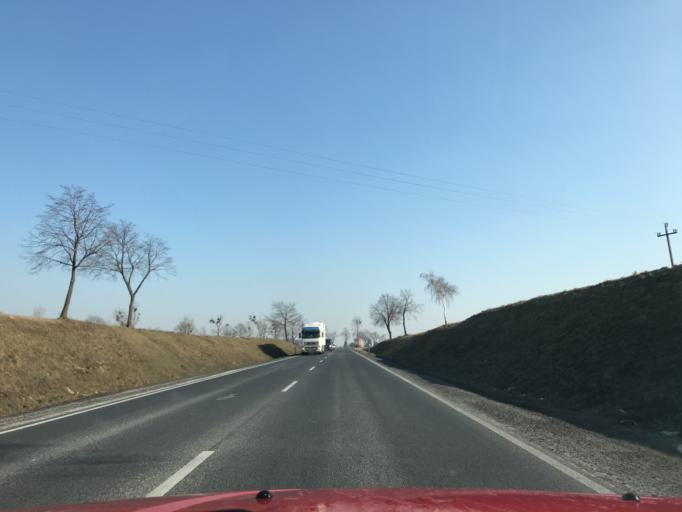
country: PL
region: Greater Poland Voivodeship
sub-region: Powiat sredzki
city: Nowe Miasto nad Warta
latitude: 52.0809
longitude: 17.4105
